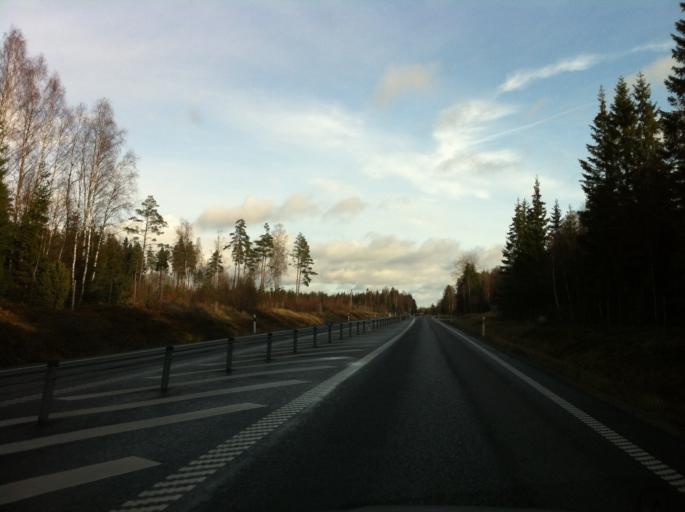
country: SE
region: Kronoberg
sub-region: Alvesta Kommun
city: Vislanda
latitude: 56.6970
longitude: 14.3444
